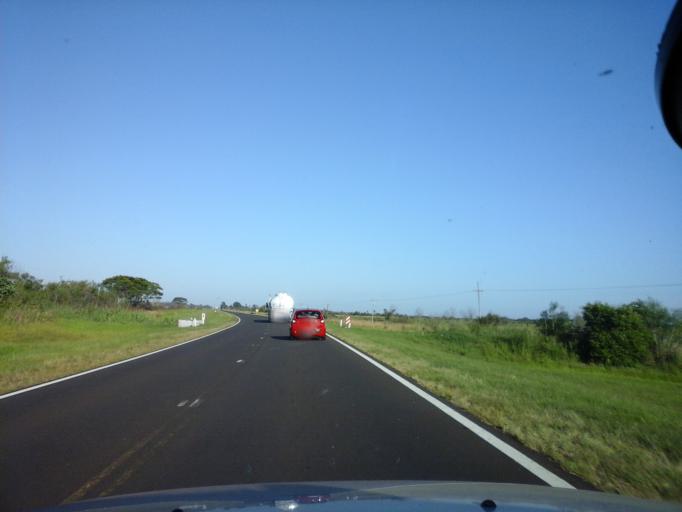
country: AR
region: Corrientes
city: Ita Ibate
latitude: -27.5027
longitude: -57.2487
